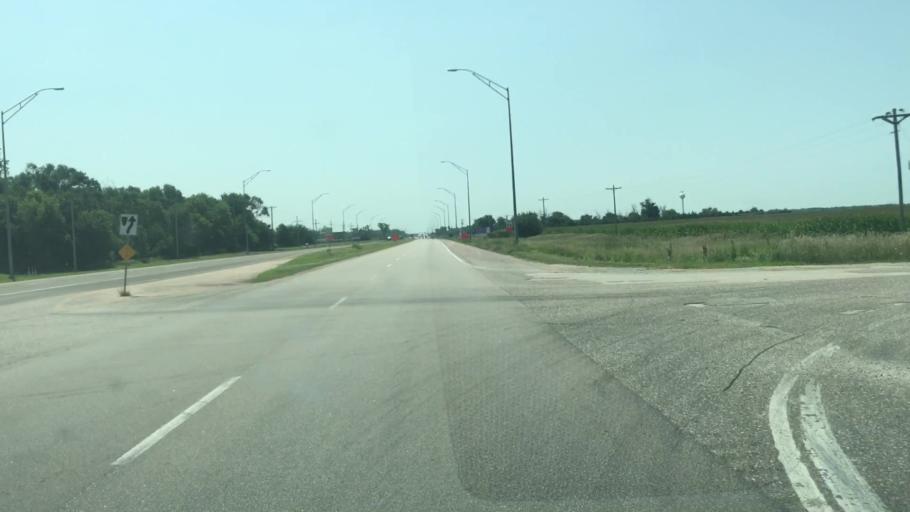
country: US
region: Nebraska
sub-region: Hall County
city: Grand Island
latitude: 40.8447
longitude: -98.3787
